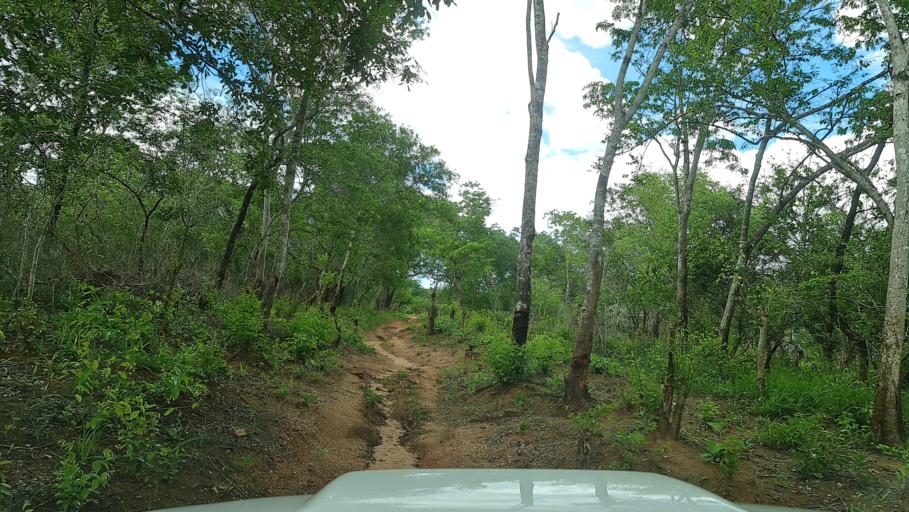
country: MZ
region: Nampula
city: Ilha de Mocambique
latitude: -15.5056
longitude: 40.1879
